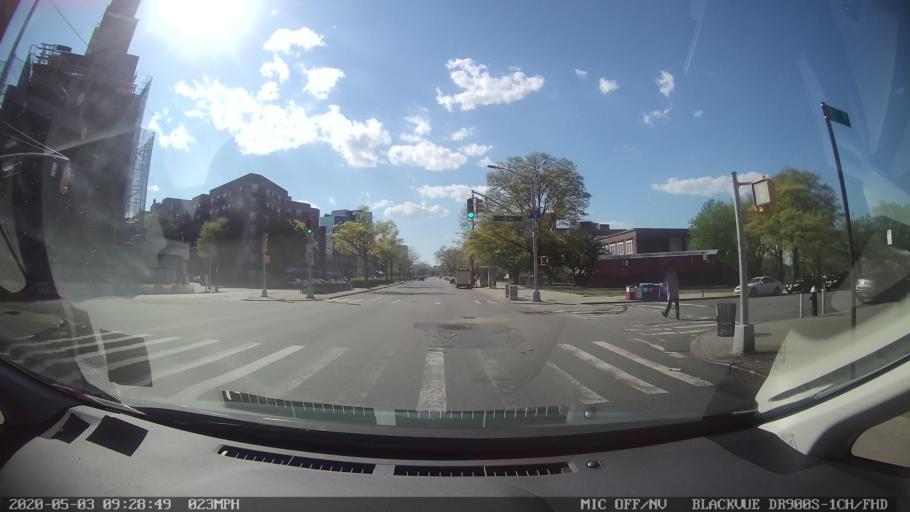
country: US
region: New York
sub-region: Queens County
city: Jamaica
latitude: 40.7127
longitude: -73.8269
